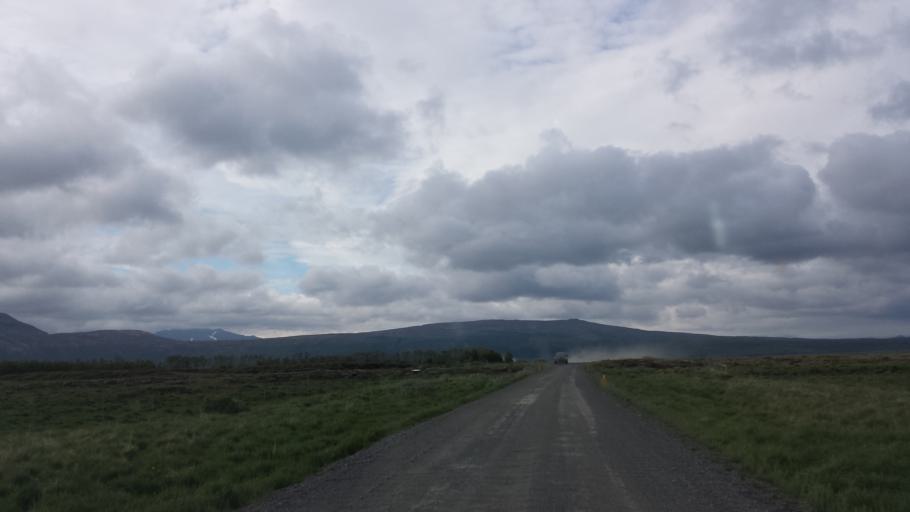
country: IS
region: South
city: Selfoss
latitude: 64.2926
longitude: -20.2354
